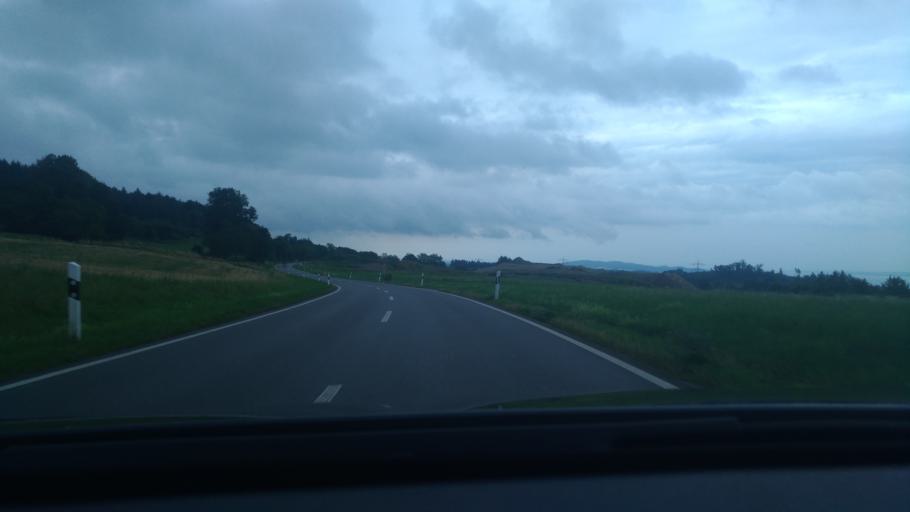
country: DE
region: Baden-Wuerttemberg
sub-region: Tuebingen Region
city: Owingen
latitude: 47.7993
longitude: 9.1376
